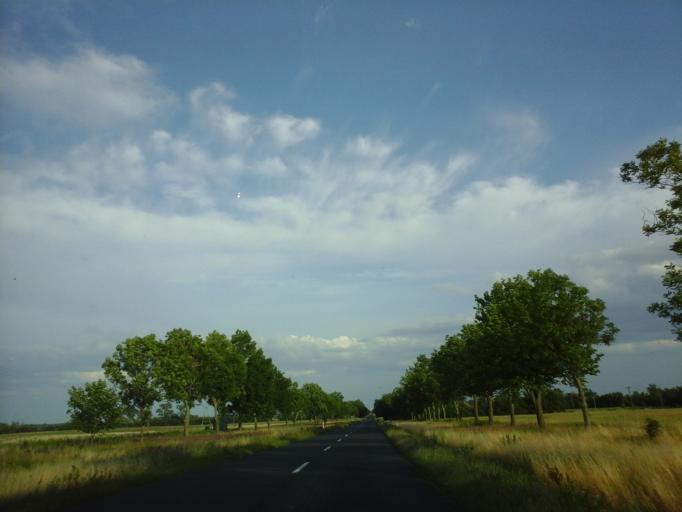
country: PL
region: West Pomeranian Voivodeship
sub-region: Powiat kamienski
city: Kamien Pomorski
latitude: 53.9492
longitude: 14.8014
